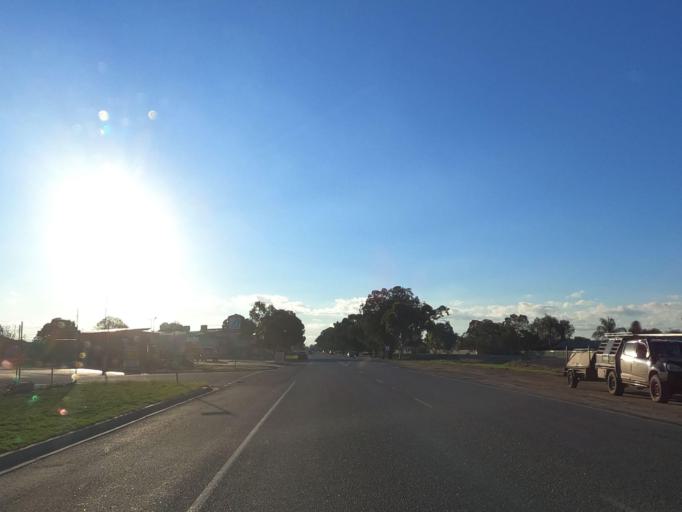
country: AU
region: Victoria
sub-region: Swan Hill
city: Swan Hill
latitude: -35.3331
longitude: 143.5587
